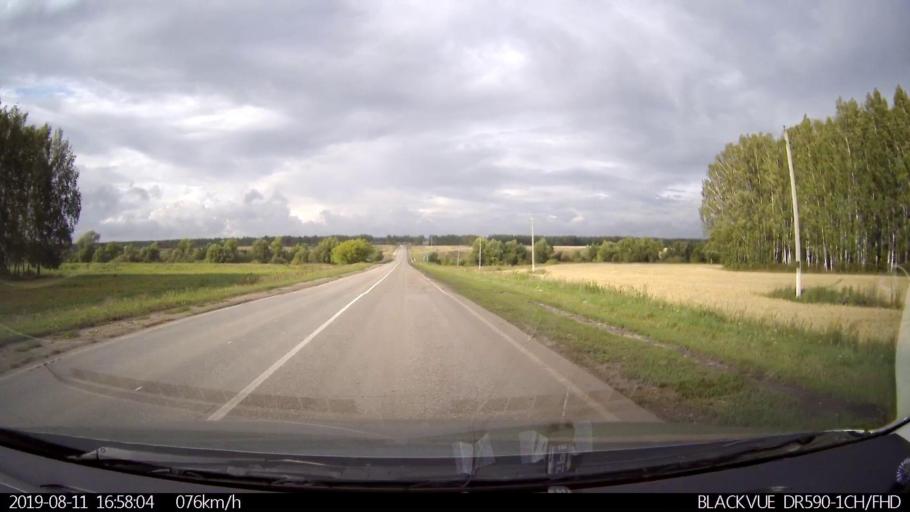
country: RU
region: Ulyanovsk
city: Mayna
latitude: 54.3047
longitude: 47.6551
